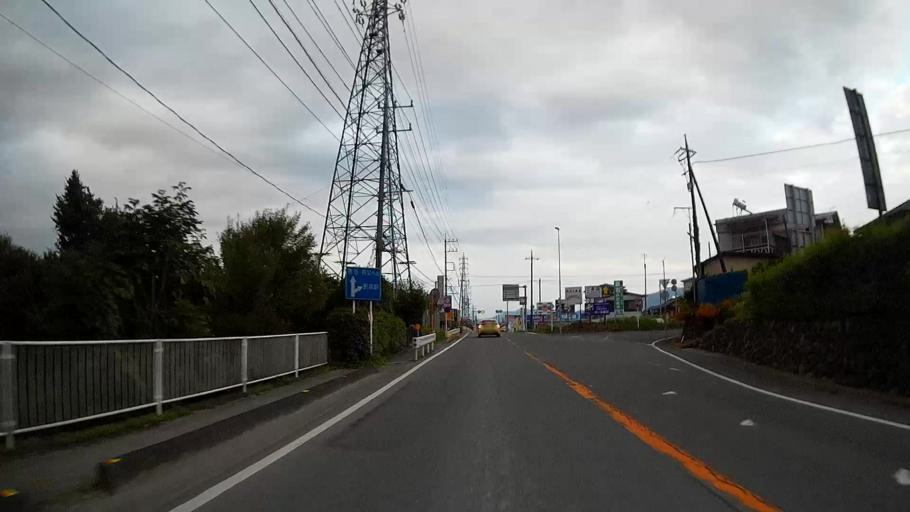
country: JP
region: Saitama
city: Chichibu
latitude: 35.9691
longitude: 139.0616
